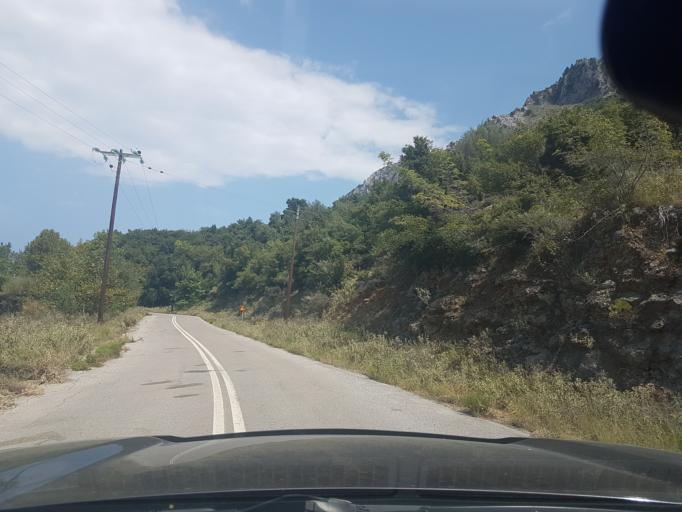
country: GR
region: Central Greece
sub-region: Nomos Evvoias
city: Kymi
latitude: 38.6382
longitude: 23.9574
